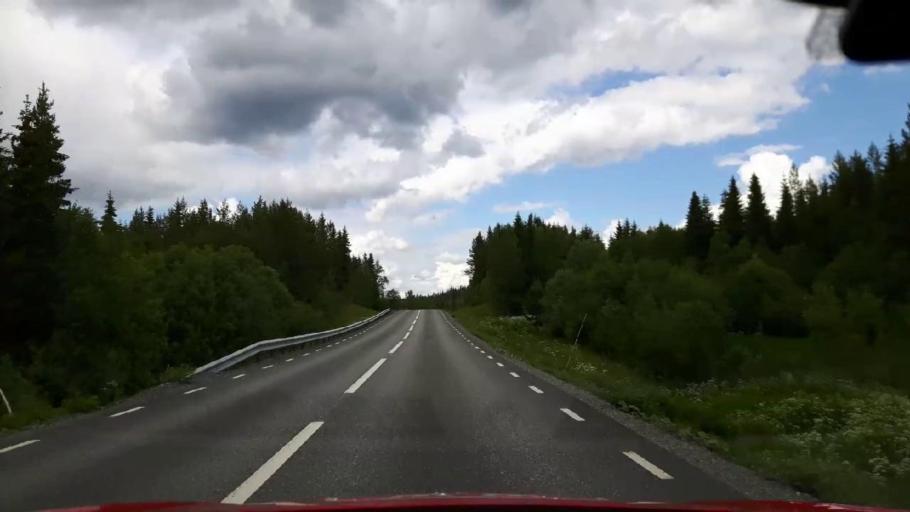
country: SE
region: Jaemtland
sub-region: Krokoms Kommun
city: Krokom
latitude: 63.7953
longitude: 14.3838
